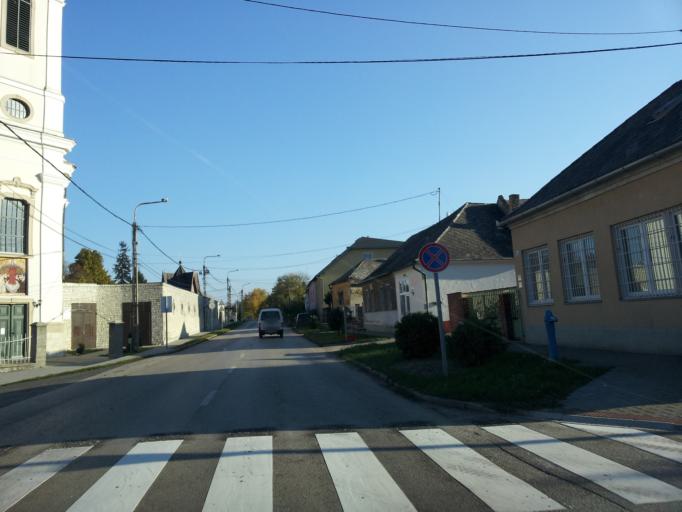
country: HU
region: Fejer
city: Bodajk
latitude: 47.3217
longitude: 18.2362
